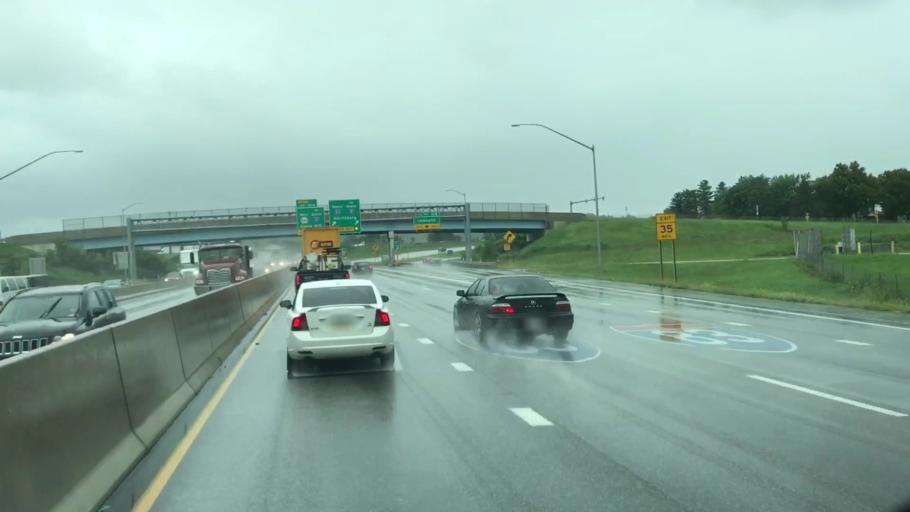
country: US
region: Pennsylvania
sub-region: Cumberland County
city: Lemoyne
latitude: 40.2347
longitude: -76.8919
